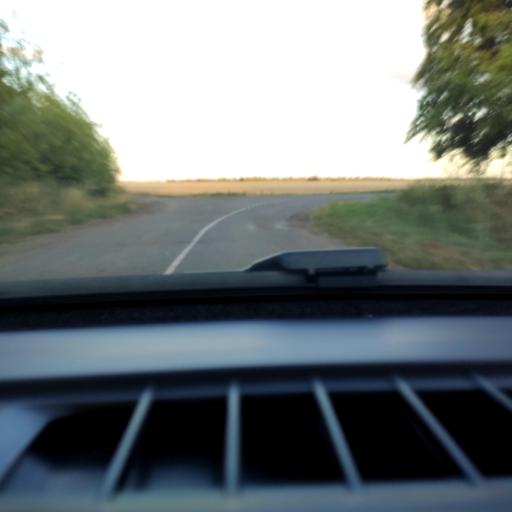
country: RU
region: Voronezj
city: Verkhnyaya Khava
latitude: 51.6113
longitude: 39.8201
